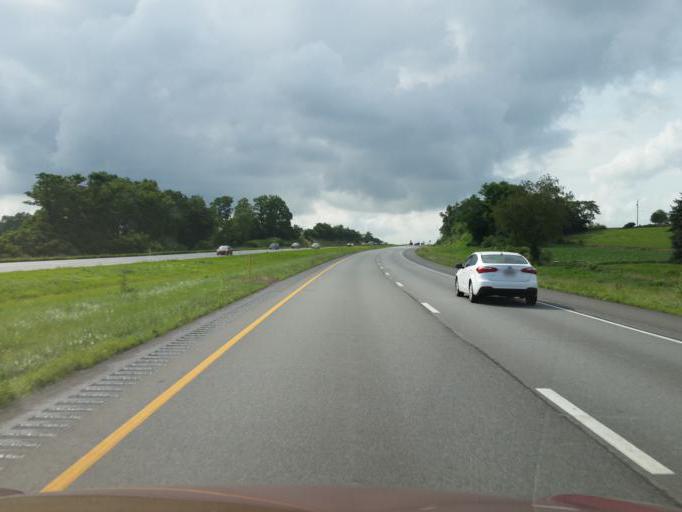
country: US
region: Pennsylvania
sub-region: Lancaster County
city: Rheems
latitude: 40.1344
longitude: -76.5430
